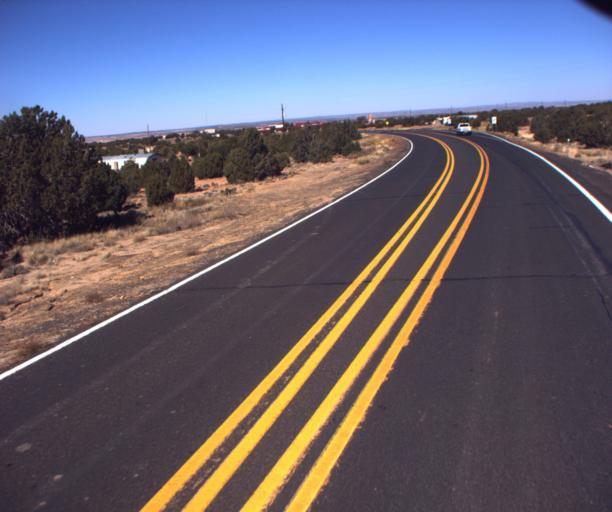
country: US
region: Arizona
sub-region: Navajo County
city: First Mesa
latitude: 35.8387
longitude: -110.5266
